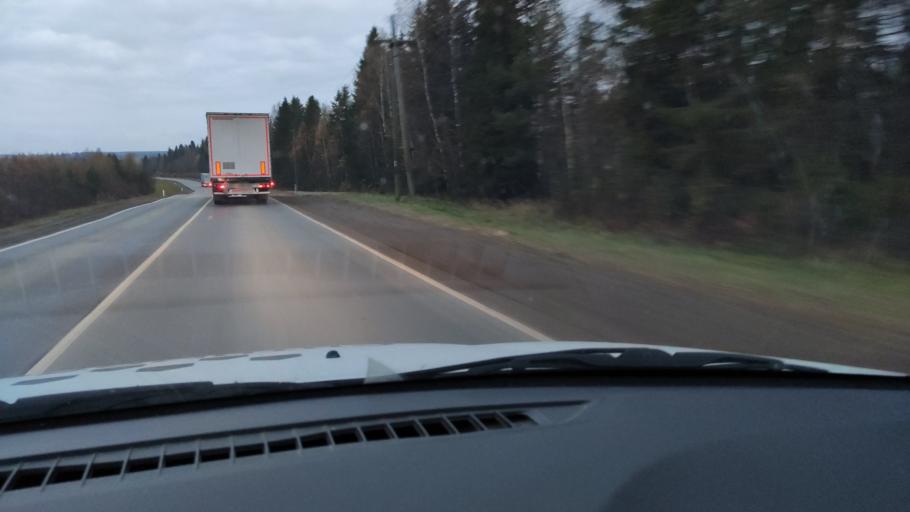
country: RU
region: Kirov
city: Kostino
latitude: 58.8564
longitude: 53.1913
